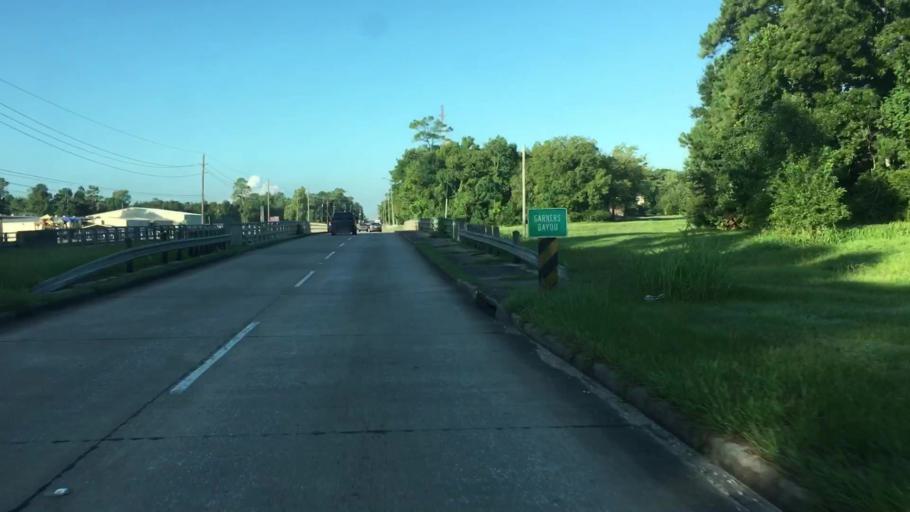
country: US
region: Texas
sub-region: Harris County
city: Humble
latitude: 29.9551
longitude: -95.2676
